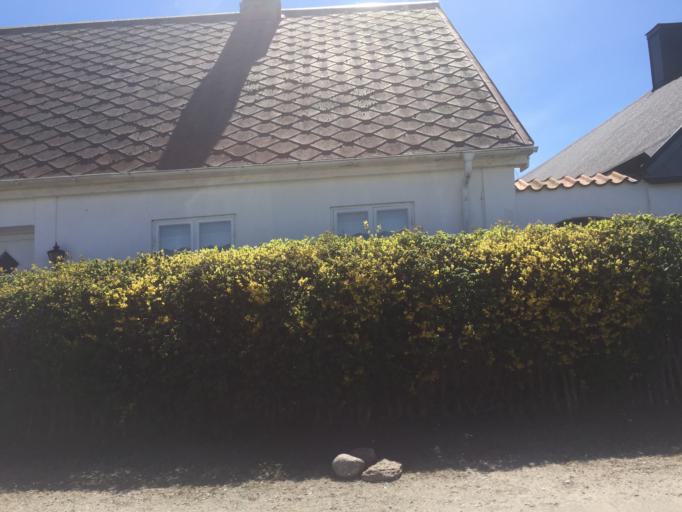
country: SE
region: Skane
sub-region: Malmo
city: Bunkeflostrand
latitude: 55.5545
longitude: 12.9617
